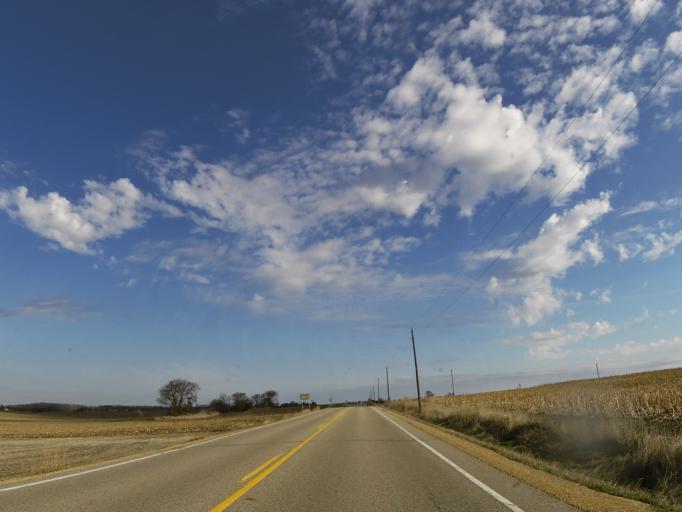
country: US
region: Minnesota
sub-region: Washington County
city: Cottage Grove
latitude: 44.8318
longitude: -92.8628
